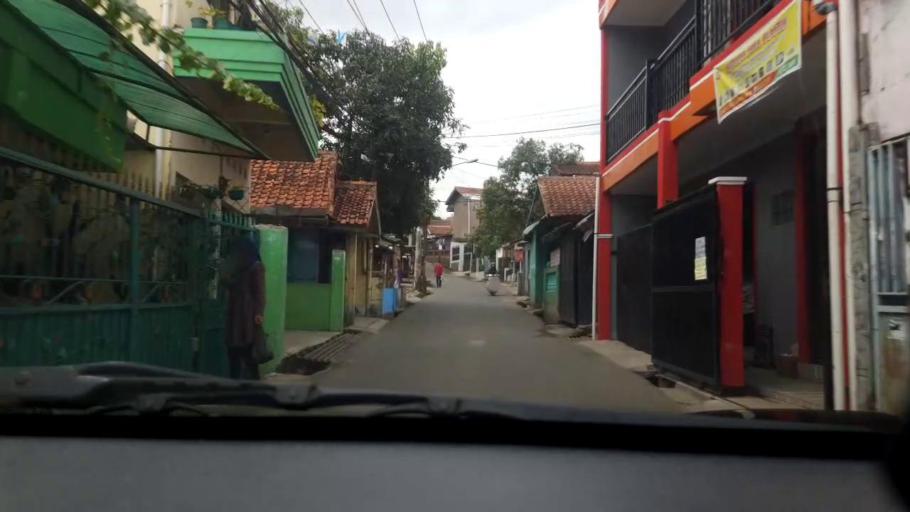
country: ID
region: West Java
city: Cileunyi
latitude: -6.9336
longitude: 107.7287
